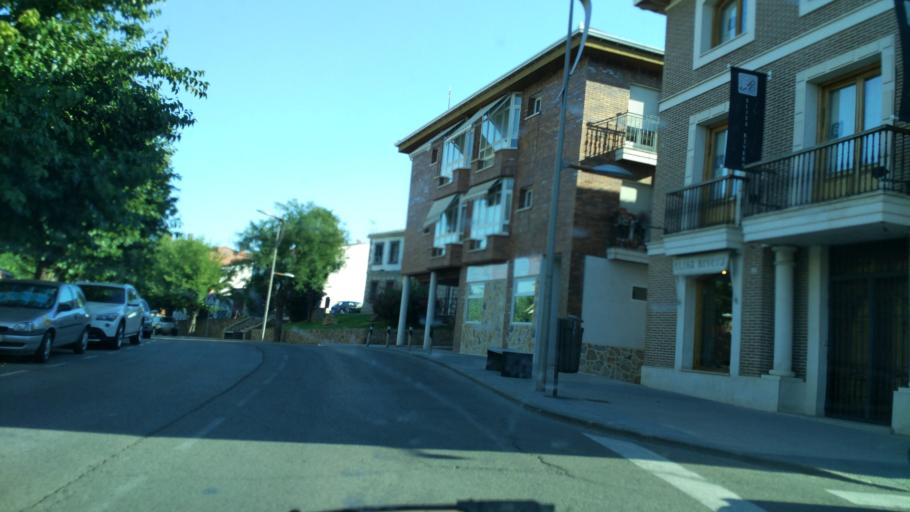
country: ES
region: Madrid
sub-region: Provincia de Madrid
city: San Agustin de Guadalix
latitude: 40.6782
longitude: -3.6148
